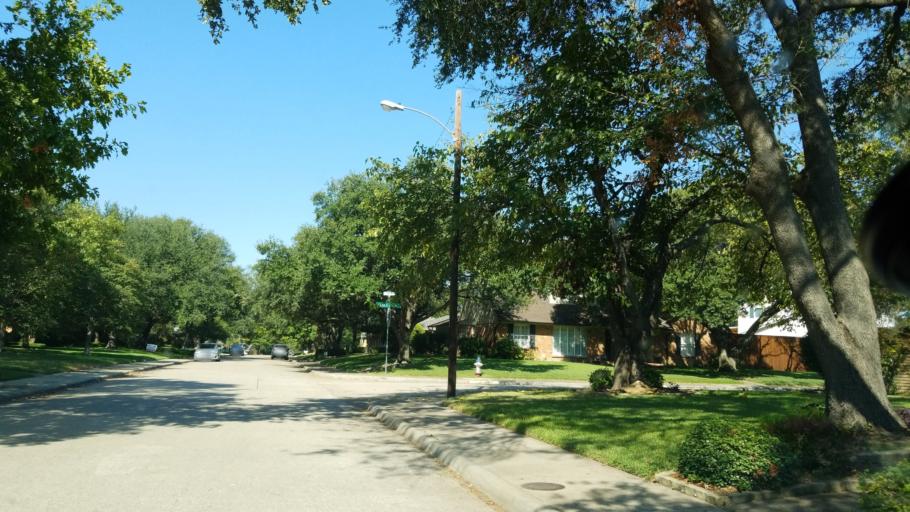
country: US
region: Texas
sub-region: Dallas County
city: Richardson
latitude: 32.9040
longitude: -96.7335
